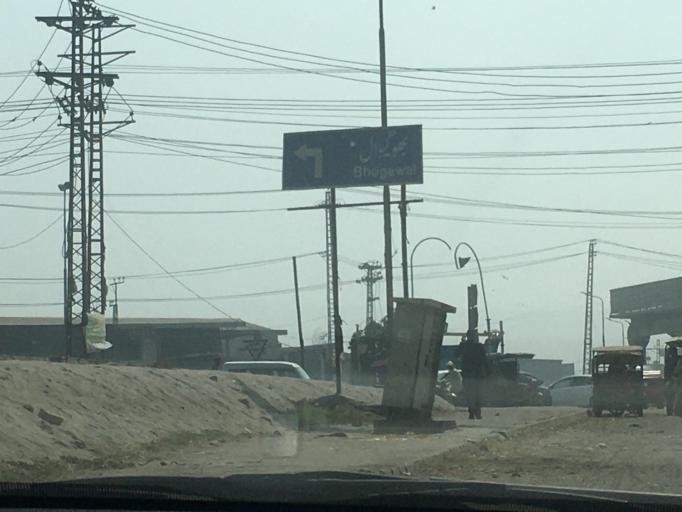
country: PK
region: Punjab
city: Lahore
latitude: 31.6095
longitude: 74.3673
